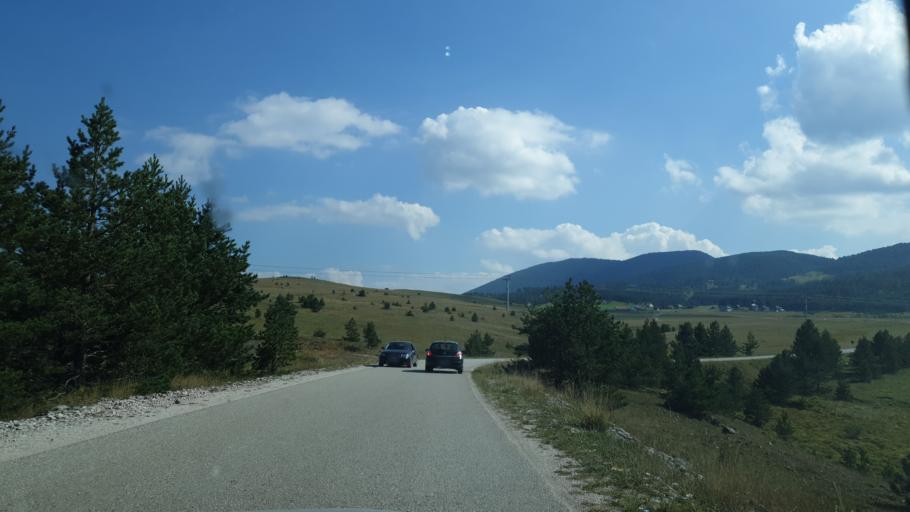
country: RS
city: Zlatibor
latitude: 43.6808
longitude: 19.6558
